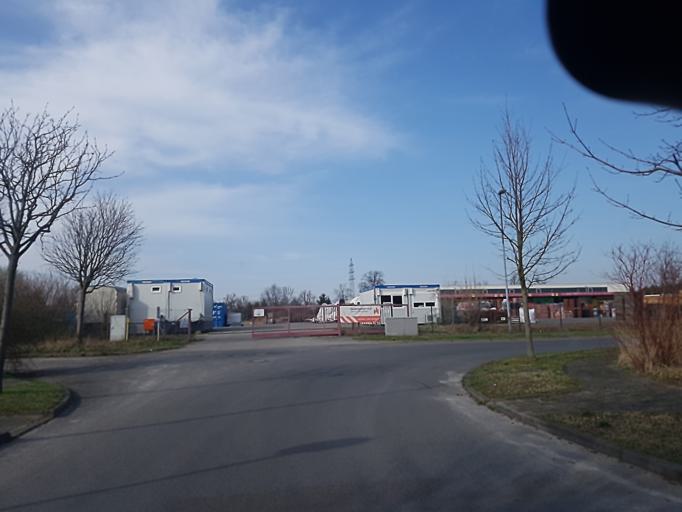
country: DE
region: Brandenburg
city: Finsterwalde
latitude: 51.6359
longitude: 13.7349
